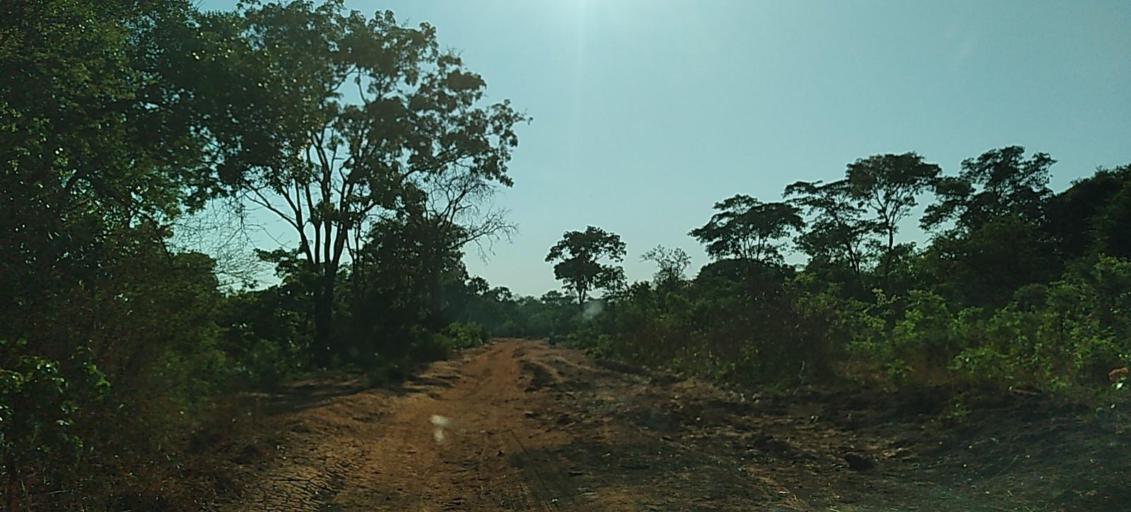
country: ZM
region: Copperbelt
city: Luanshya
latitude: -13.4592
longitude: 28.8133
